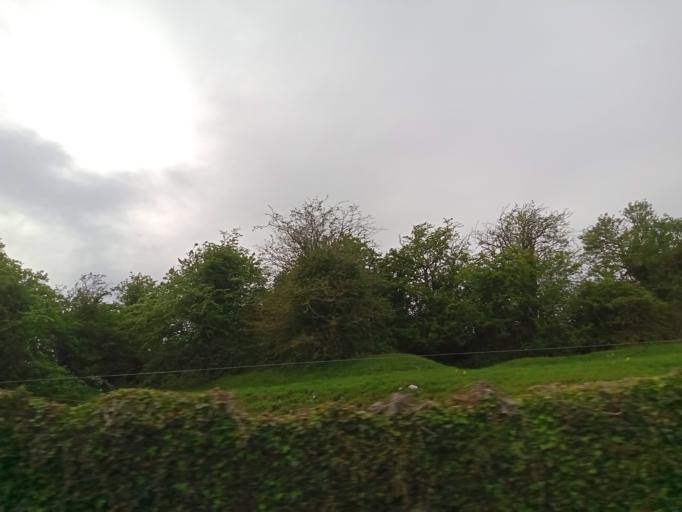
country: IE
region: Leinster
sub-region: Laois
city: Rathdowney
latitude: 52.7106
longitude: -7.4918
